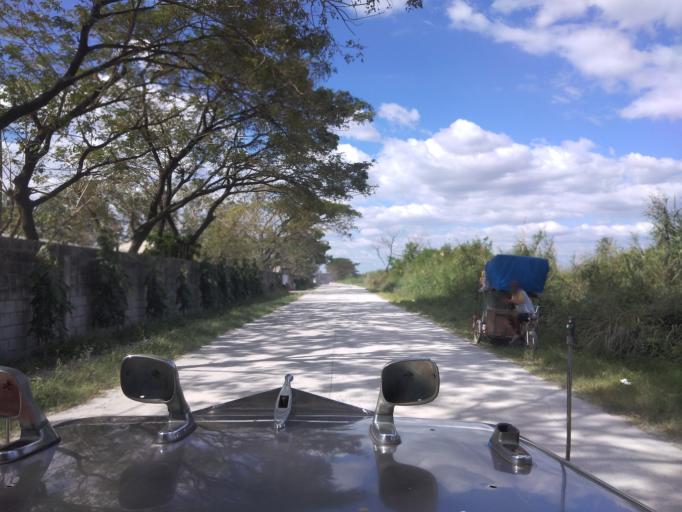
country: PH
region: Central Luzon
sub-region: Province of Pampanga
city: Magliman
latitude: 15.0379
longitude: 120.6317
